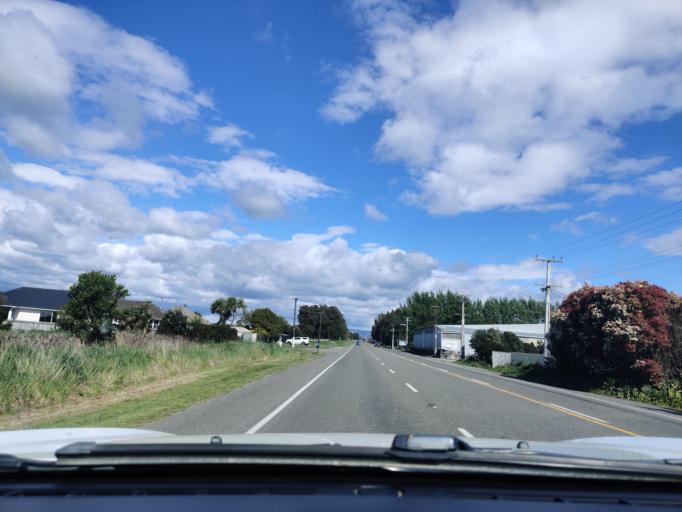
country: NZ
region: Manawatu-Wanganui
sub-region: Palmerston North City
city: Palmerston North
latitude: -40.2947
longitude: 175.5381
